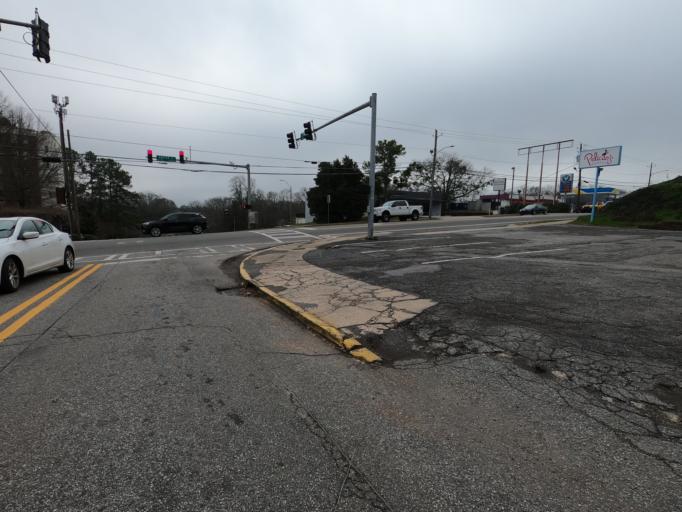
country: US
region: Georgia
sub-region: Clarke County
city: Athens
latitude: 33.9503
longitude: -83.3838
